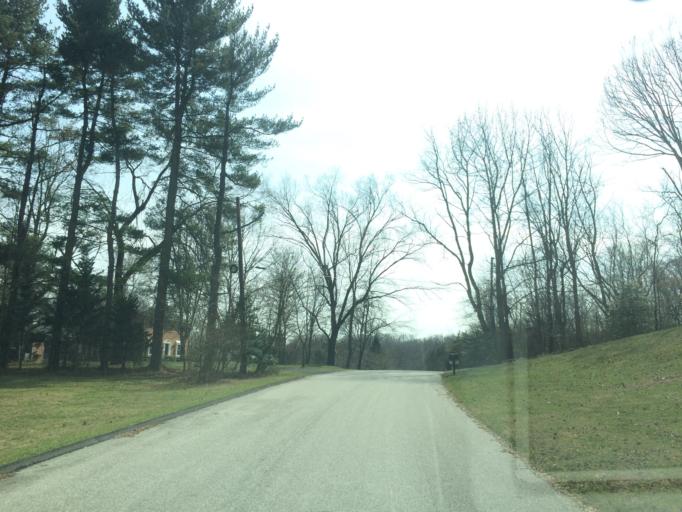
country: US
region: Maryland
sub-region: Howard County
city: Riverside
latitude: 39.1858
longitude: -76.9119
